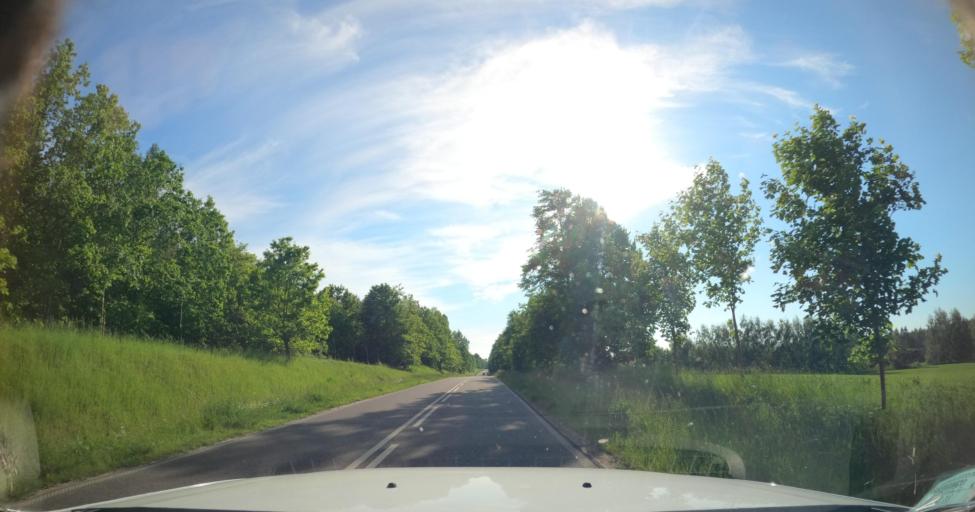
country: PL
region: Warmian-Masurian Voivodeship
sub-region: Powiat elblaski
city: Paslek
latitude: 54.0772
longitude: 19.7074
